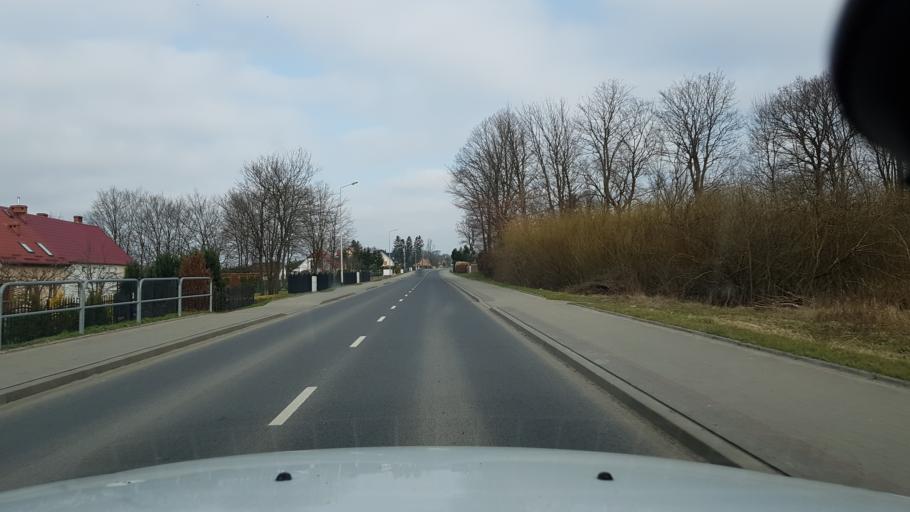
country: PL
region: West Pomeranian Voivodeship
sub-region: Powiat koszalinski
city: Sianow
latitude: 54.2517
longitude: 16.2785
